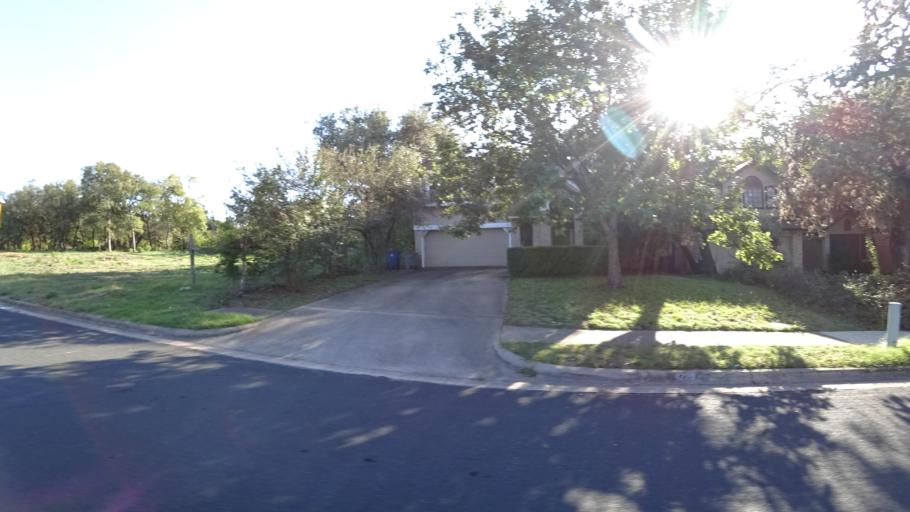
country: US
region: Texas
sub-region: Travis County
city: Shady Hollow
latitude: 30.2040
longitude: -97.8492
